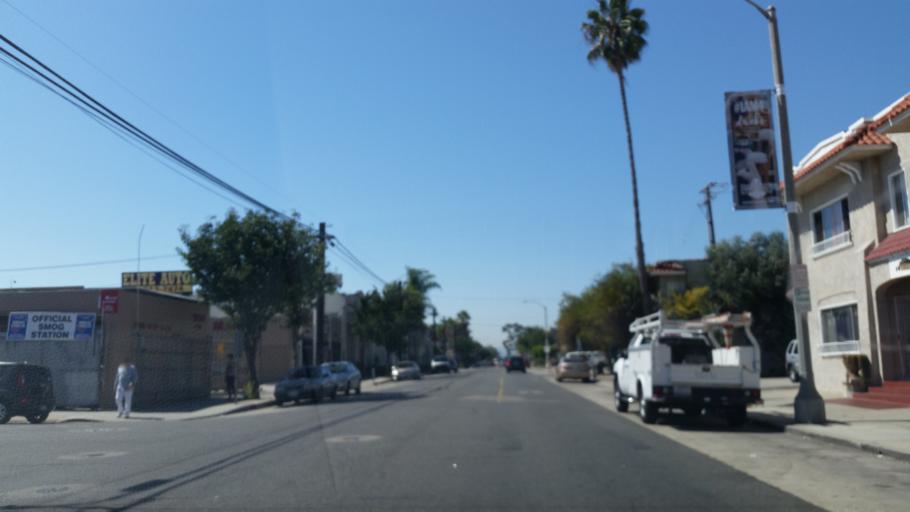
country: US
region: California
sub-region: Los Angeles County
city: Long Beach
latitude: 33.7718
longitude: -118.1692
